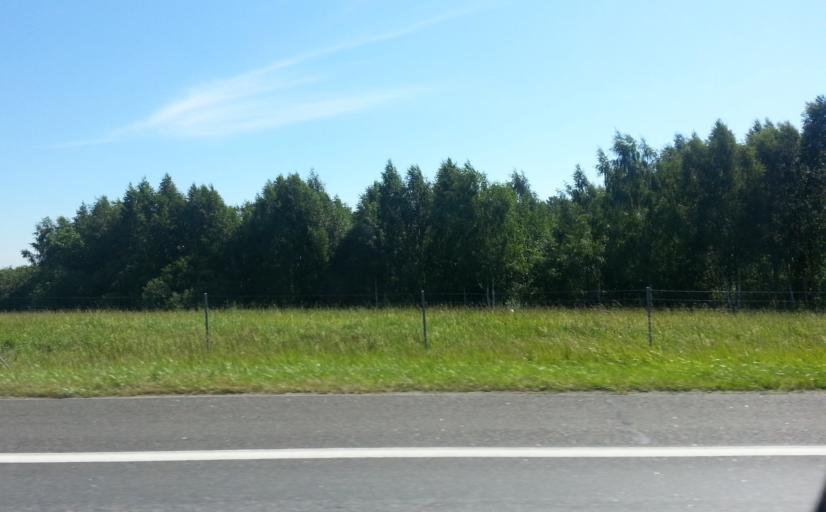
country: LT
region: Vilnius County
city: Ukmerge
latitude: 55.4403
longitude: 24.6732
